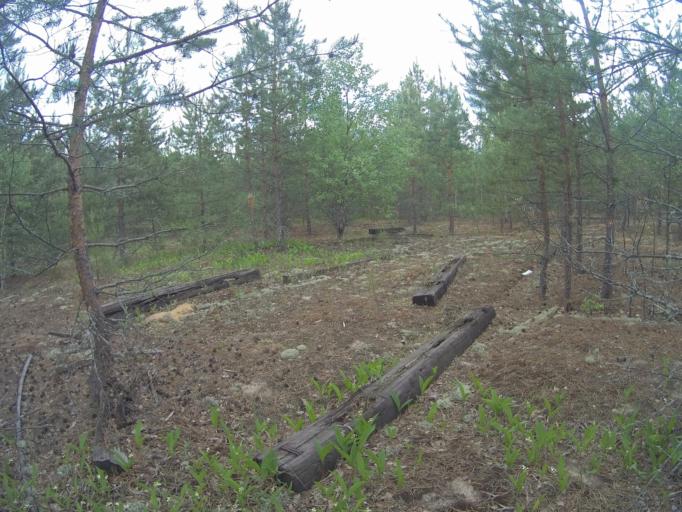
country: RU
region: Vladimir
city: Raduzhnyy
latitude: 55.9709
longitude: 40.2634
